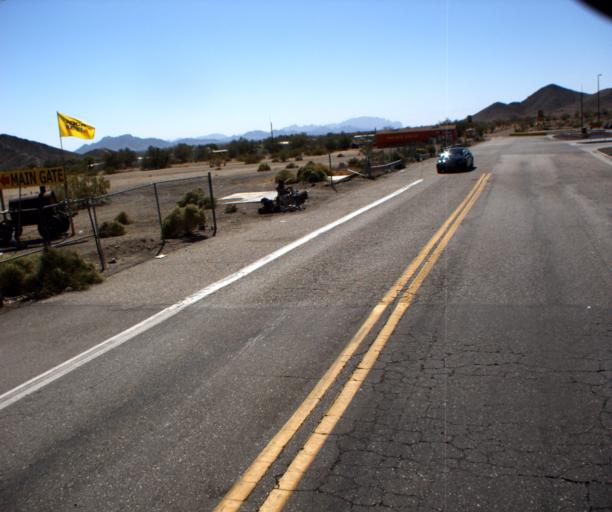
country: US
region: Arizona
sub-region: La Paz County
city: Quartzsite
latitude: 33.6578
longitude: -114.2405
